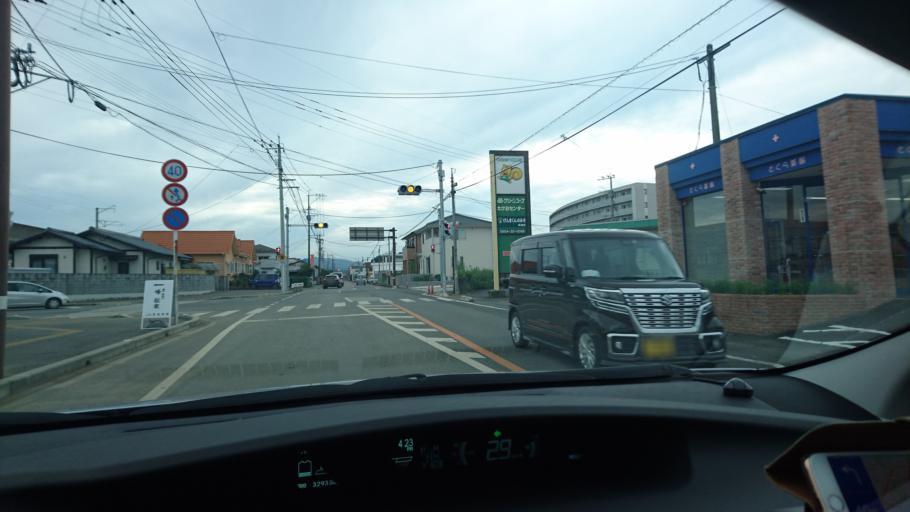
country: JP
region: Saga Prefecture
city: Takeocho-takeo
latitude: 33.2019
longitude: 130.0314
